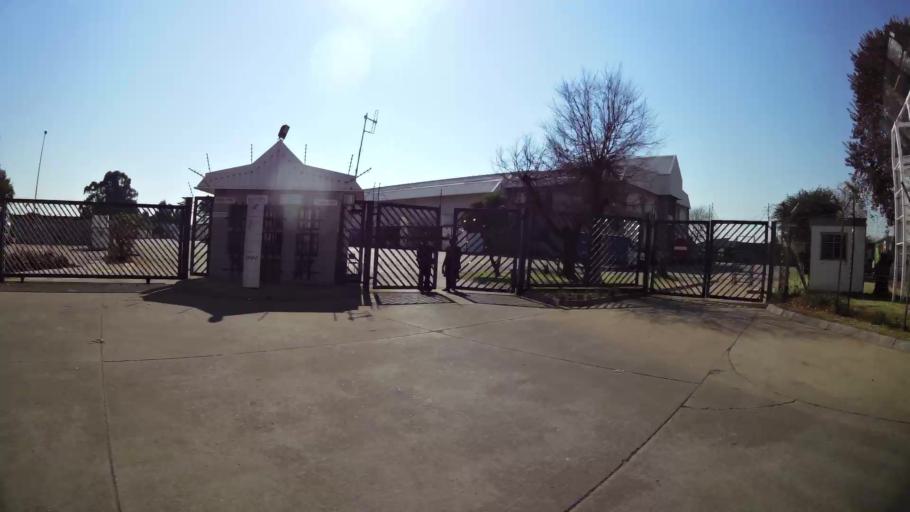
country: ZA
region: Gauteng
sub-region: Ekurhuleni Metropolitan Municipality
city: Boksburg
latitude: -26.1763
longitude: 28.2152
